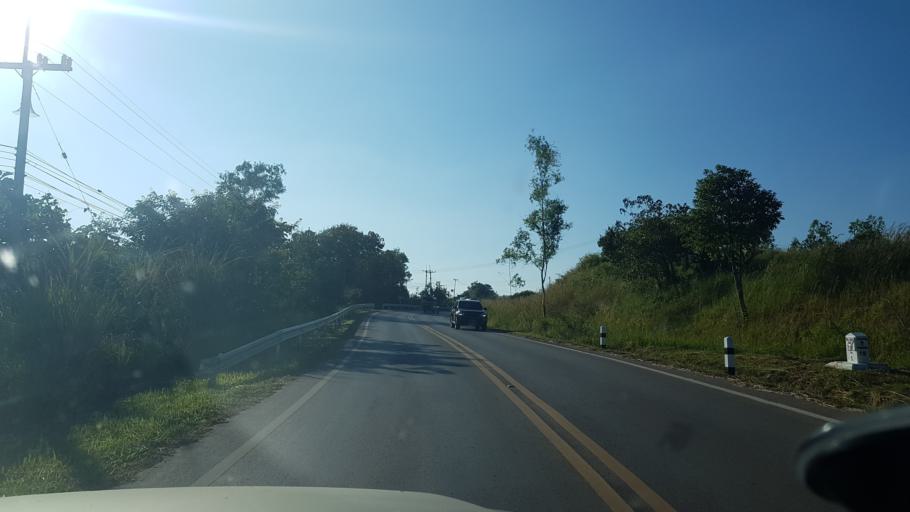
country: TH
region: Phetchabun
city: Khao Kho
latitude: 16.6480
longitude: 101.0031
